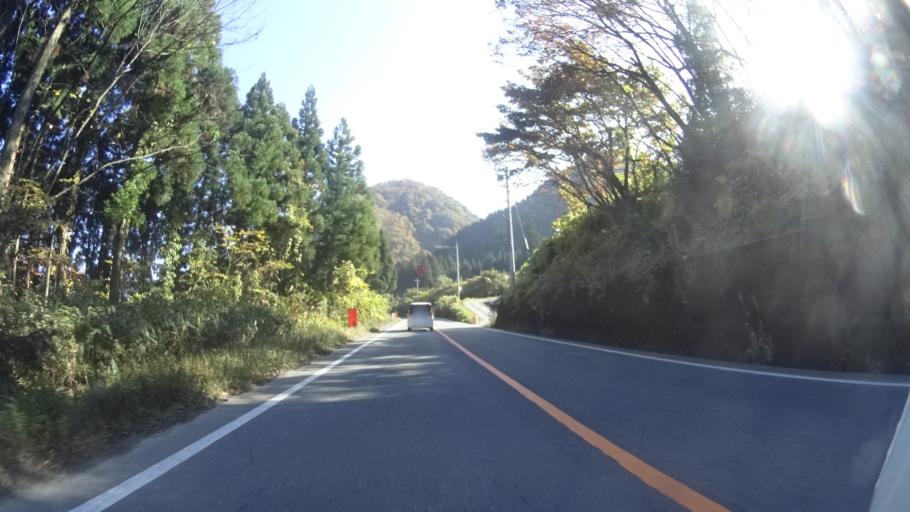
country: JP
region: Fukui
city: Ono
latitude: 35.9708
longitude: 136.5681
